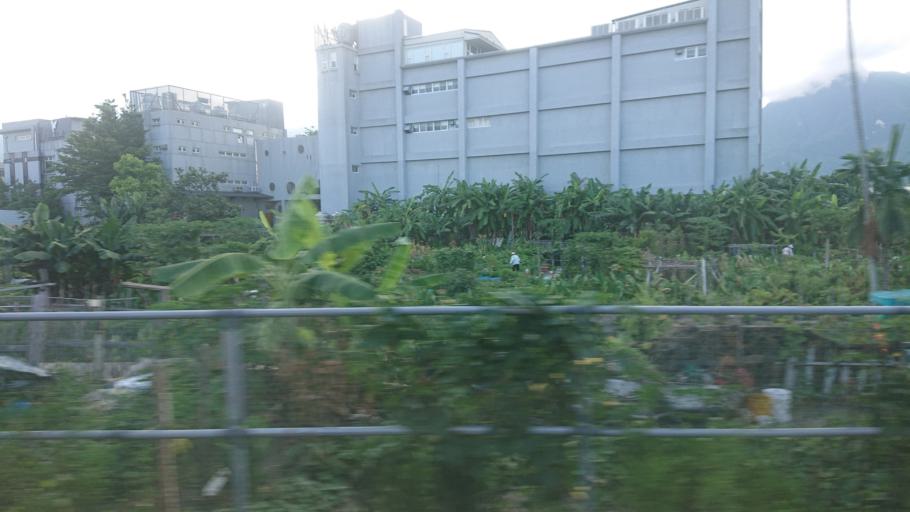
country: TW
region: Taiwan
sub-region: Hualien
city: Hualian
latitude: 23.9771
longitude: 121.5932
